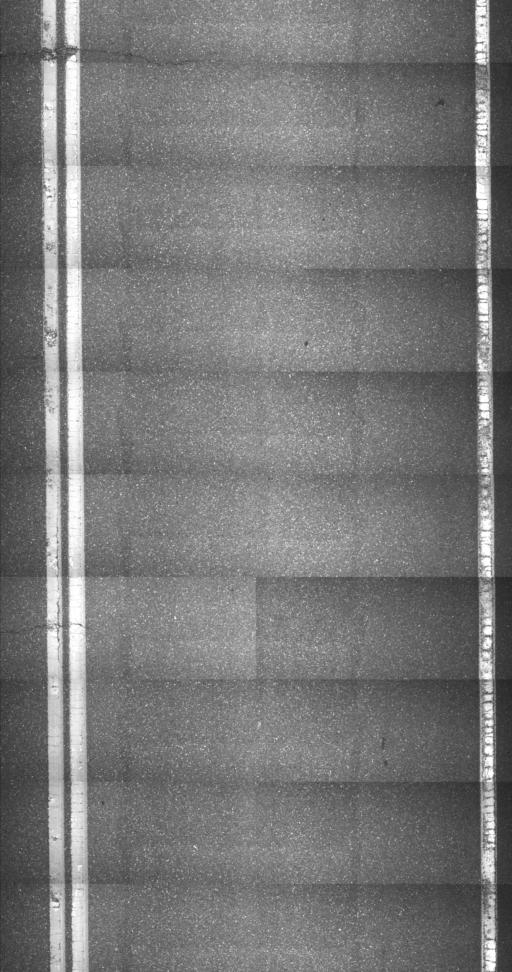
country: US
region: Vermont
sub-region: Orleans County
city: Newport
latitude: 45.0045
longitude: -72.4143
